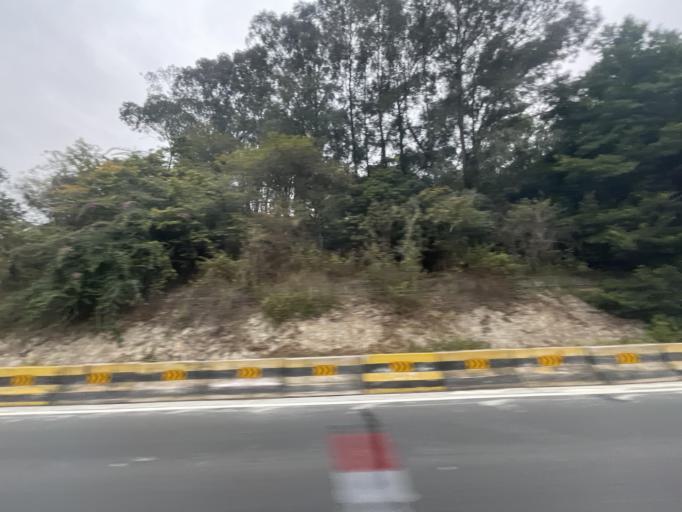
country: CN
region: Guangdong
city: Humen
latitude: 22.8068
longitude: 113.6593
